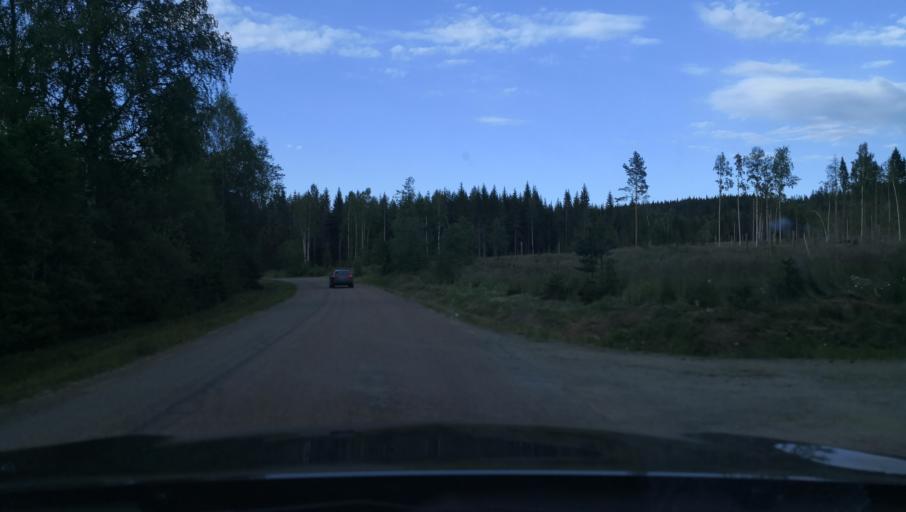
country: SE
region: Dalarna
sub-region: Ludvika Kommun
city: Ludvika
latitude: 60.0852
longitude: 15.2709
